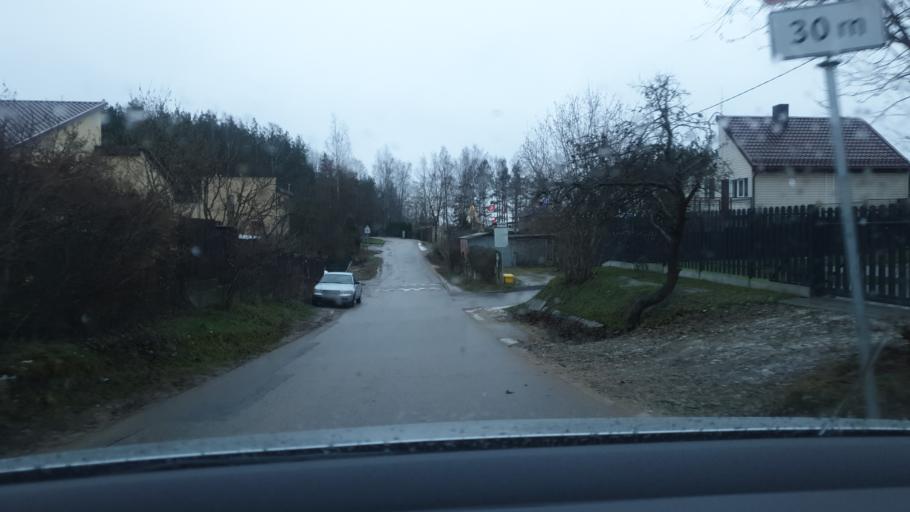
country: LT
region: Vilnius County
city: Rasos
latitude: 54.7200
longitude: 25.3869
